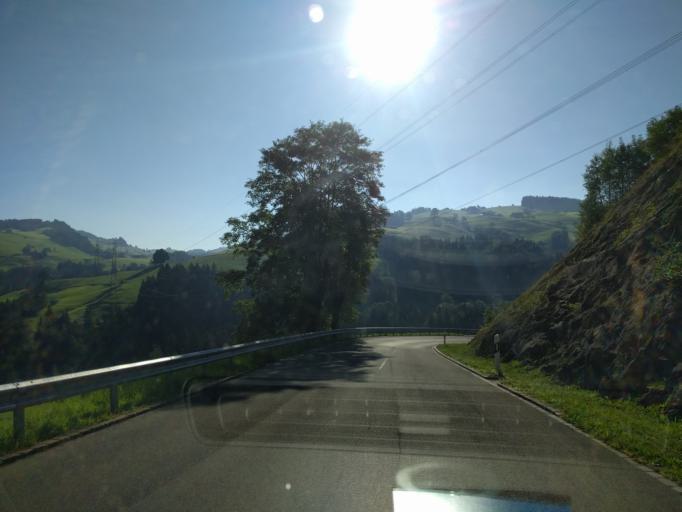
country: CH
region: Saint Gallen
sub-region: Wahlkreis Toggenburg
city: Sankt Peterzell
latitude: 47.2927
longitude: 9.1814
